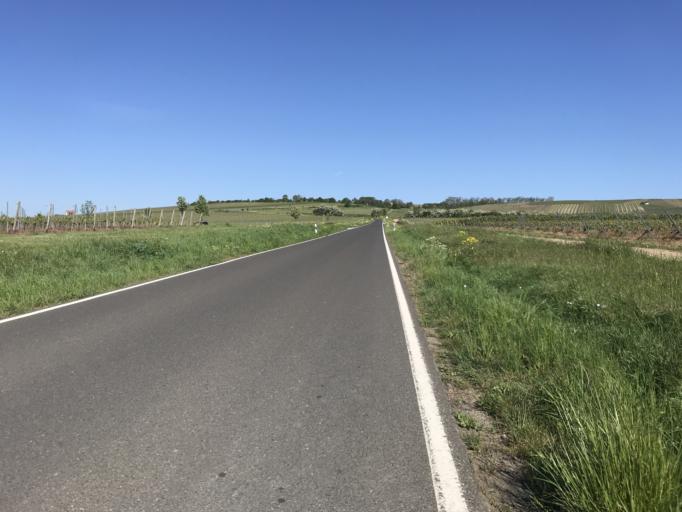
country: DE
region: Rheinland-Pfalz
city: Hahnheim
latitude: 49.8699
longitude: 8.2231
